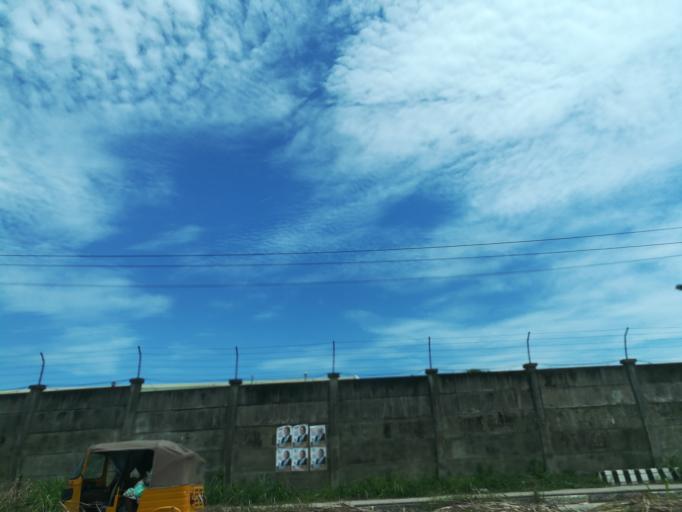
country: NG
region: Lagos
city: Ebute Ikorodu
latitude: 6.5744
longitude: 3.4864
